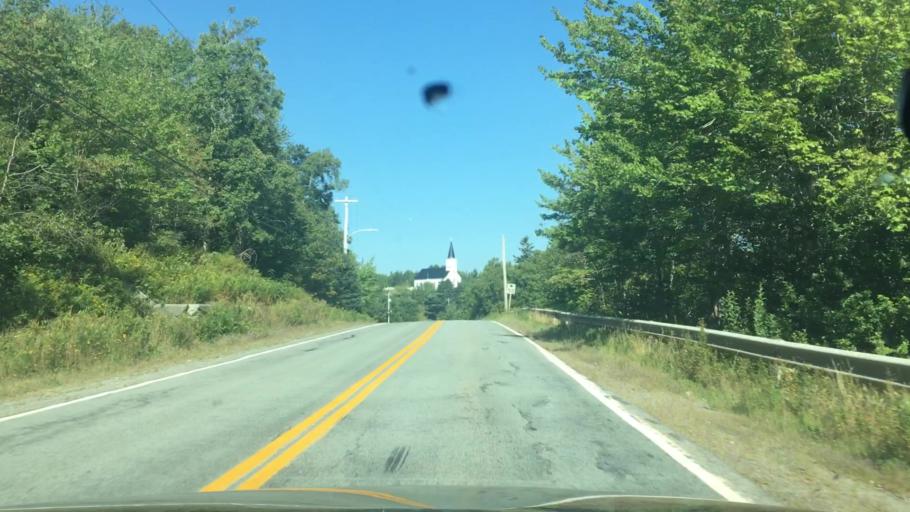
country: CA
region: Nova Scotia
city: New Glasgow
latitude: 44.9206
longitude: -62.5439
